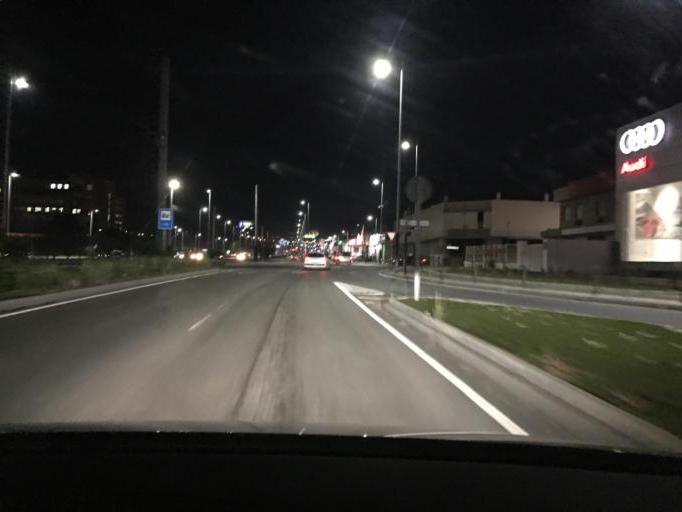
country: ES
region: Andalusia
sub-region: Provincia de Jaen
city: Jaen
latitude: 37.7984
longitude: -3.7790
